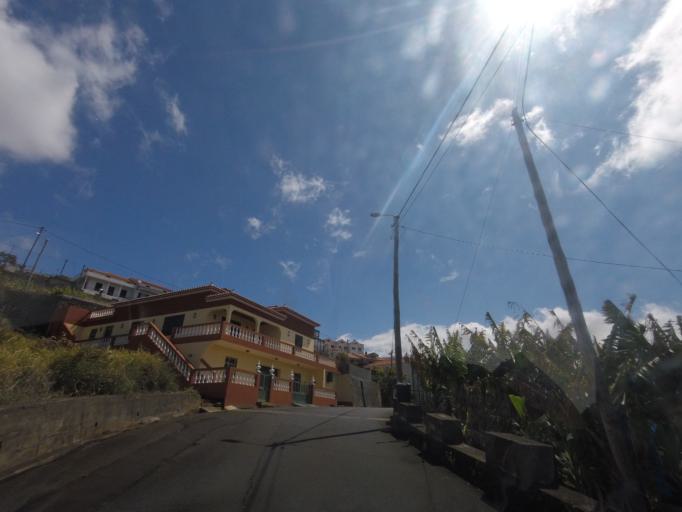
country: PT
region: Madeira
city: Ponta do Sol
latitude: 32.6840
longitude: -17.0804
